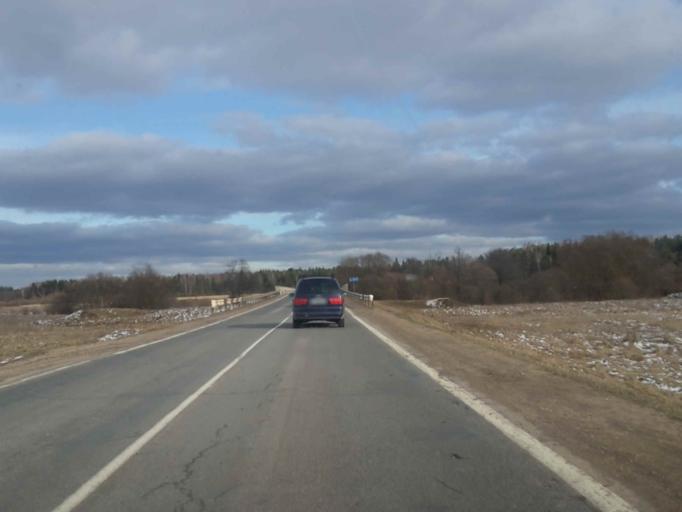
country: BY
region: Minsk
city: Il'ya
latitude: 54.4118
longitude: 27.2954
